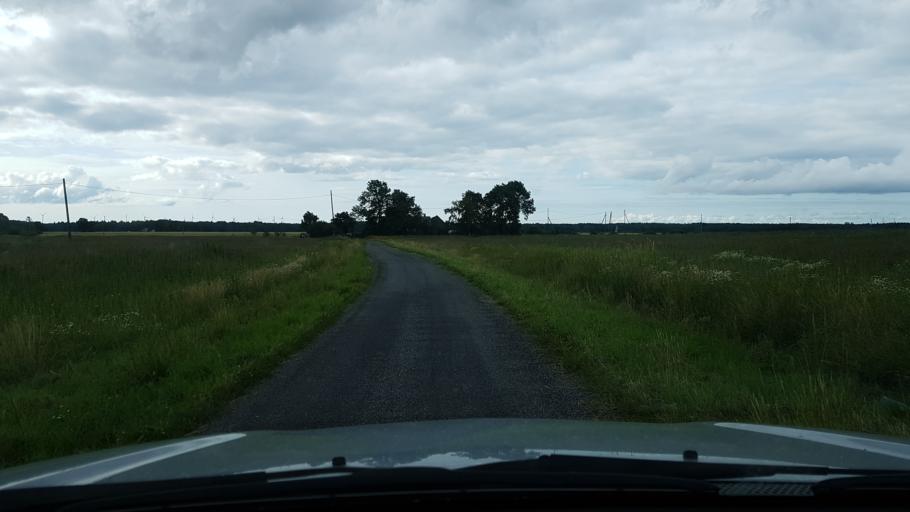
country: EE
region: Ida-Virumaa
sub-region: Narva-Joesuu linn
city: Narva-Joesuu
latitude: 59.3953
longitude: 28.0048
